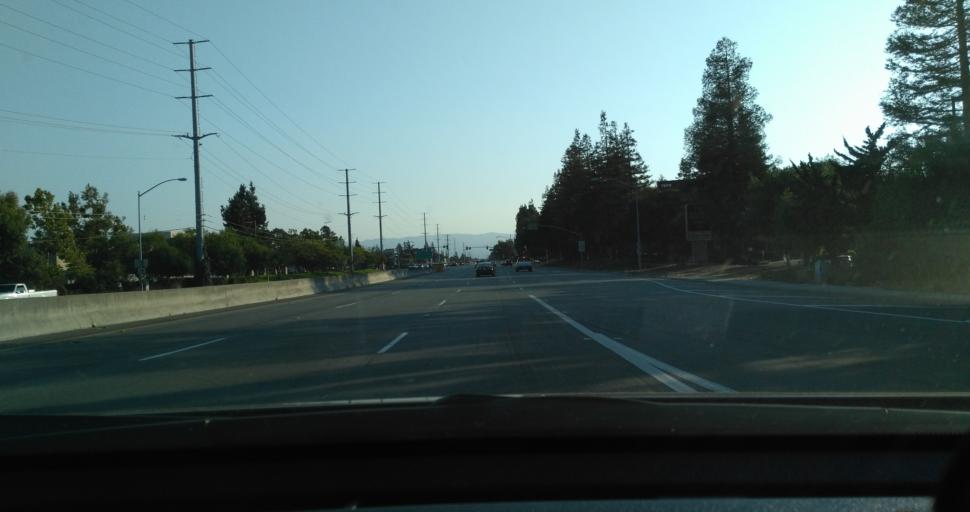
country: US
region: California
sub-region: Santa Clara County
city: Milpitas
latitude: 37.4001
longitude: -121.9108
